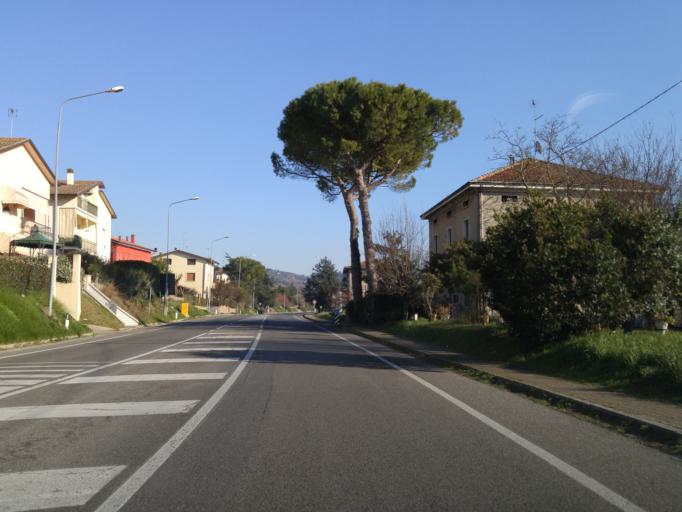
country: IT
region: The Marches
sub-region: Provincia di Pesaro e Urbino
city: Gradara
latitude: 43.9477
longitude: 12.7960
